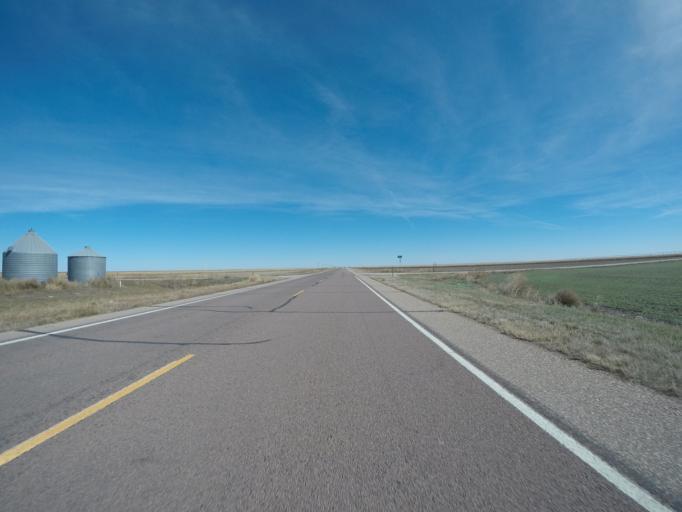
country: US
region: Colorado
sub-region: Kit Carson County
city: Burlington
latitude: 39.6578
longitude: -102.4810
